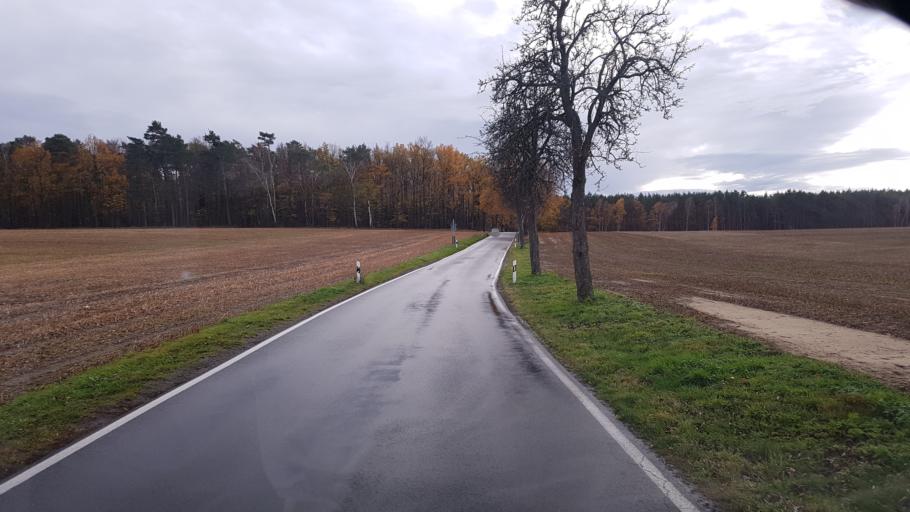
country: DE
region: Brandenburg
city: Ortrand
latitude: 51.3560
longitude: 13.7448
